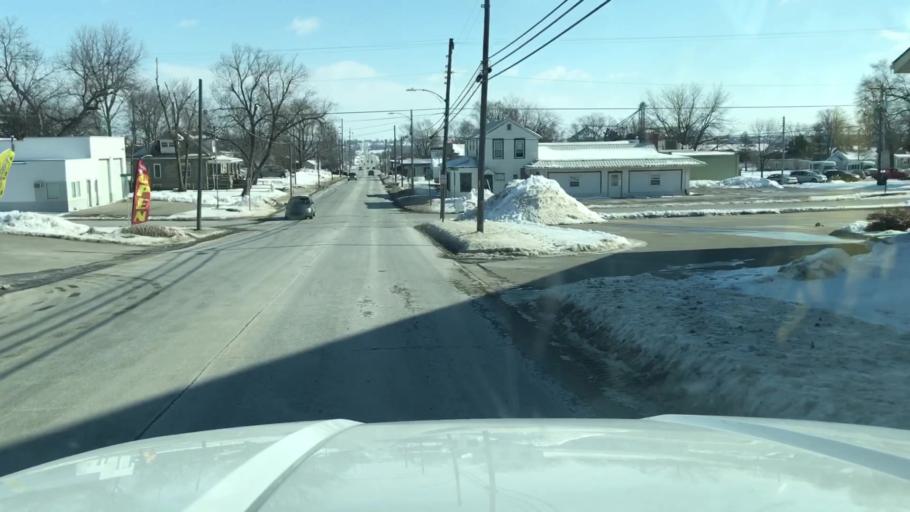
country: US
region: Missouri
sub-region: Nodaway County
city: Maryville
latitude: 40.3454
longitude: -94.8605
